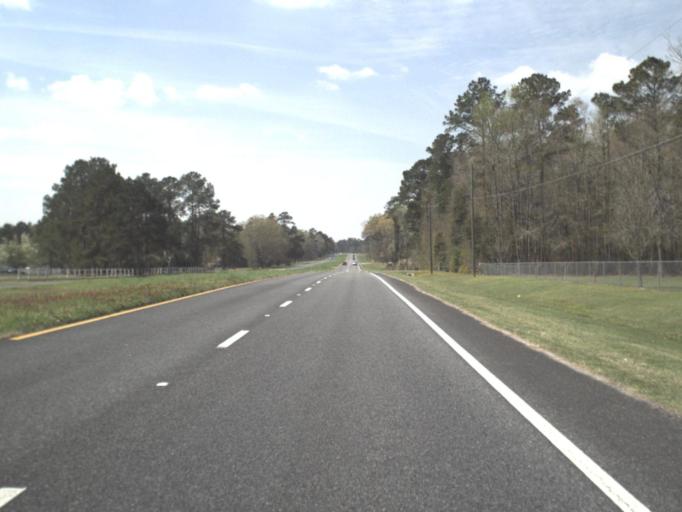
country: US
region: Florida
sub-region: Gadsden County
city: Havana
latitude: 30.6734
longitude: -84.3921
